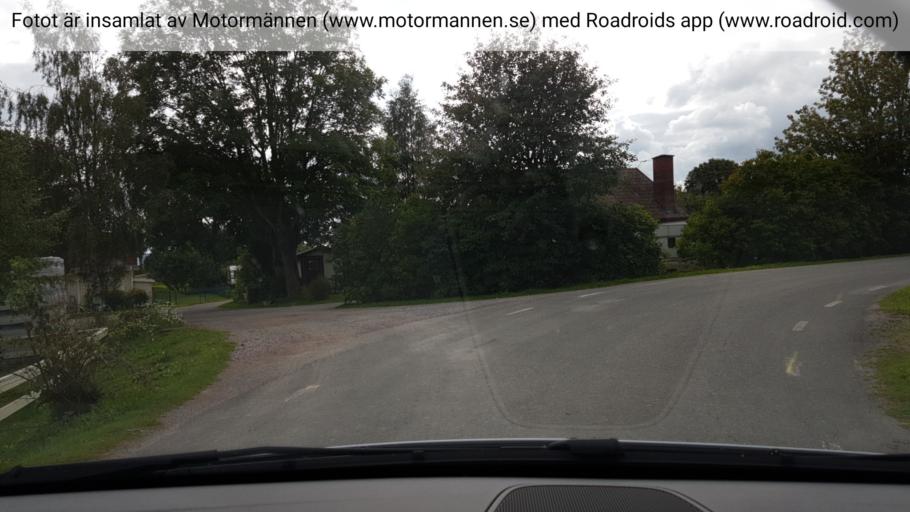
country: SE
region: Vaestra Goetaland
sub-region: Skovde Kommun
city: Skultorp
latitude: 58.2921
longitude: 13.7976
